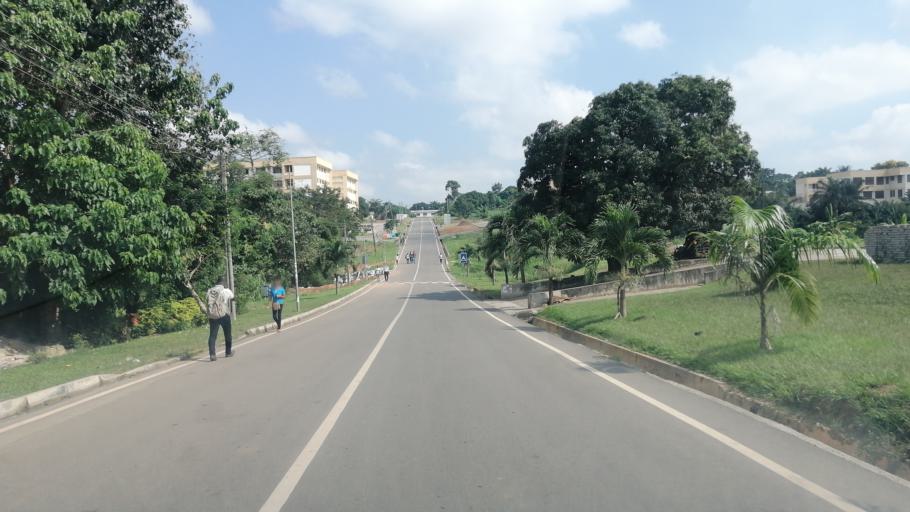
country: GH
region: Ashanti
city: Kumasi
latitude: 6.6986
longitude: -1.6821
